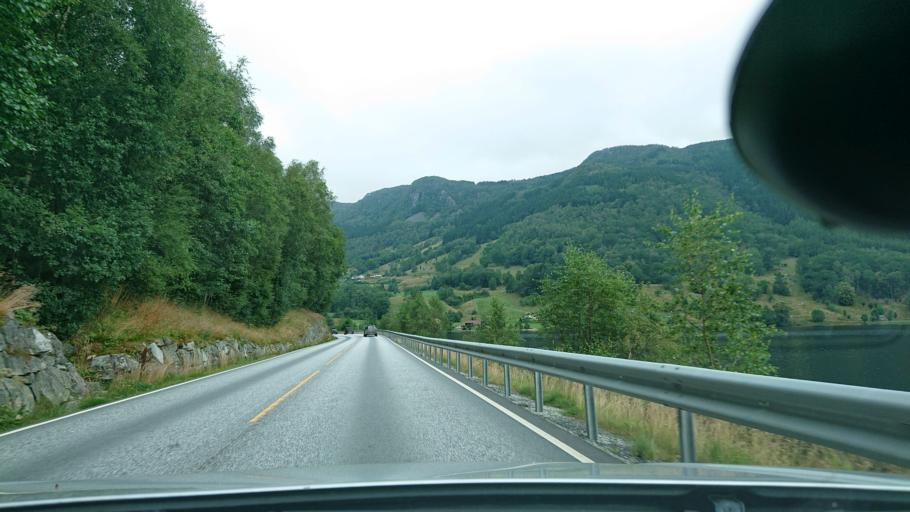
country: NO
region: Rogaland
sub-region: Hjelmeland
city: Hjelmelandsvagen
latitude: 59.1608
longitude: 6.1744
